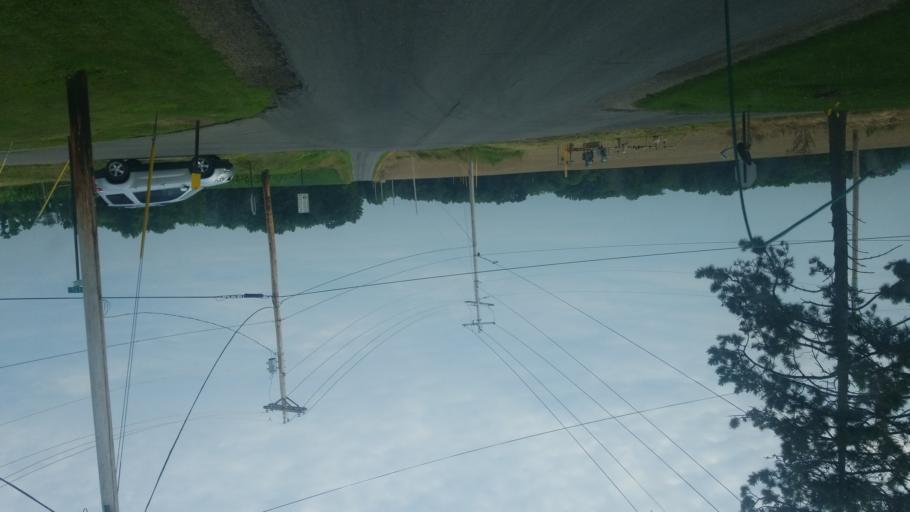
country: US
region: Ohio
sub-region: Wayne County
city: Wooster
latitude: 40.7855
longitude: -82.0231
